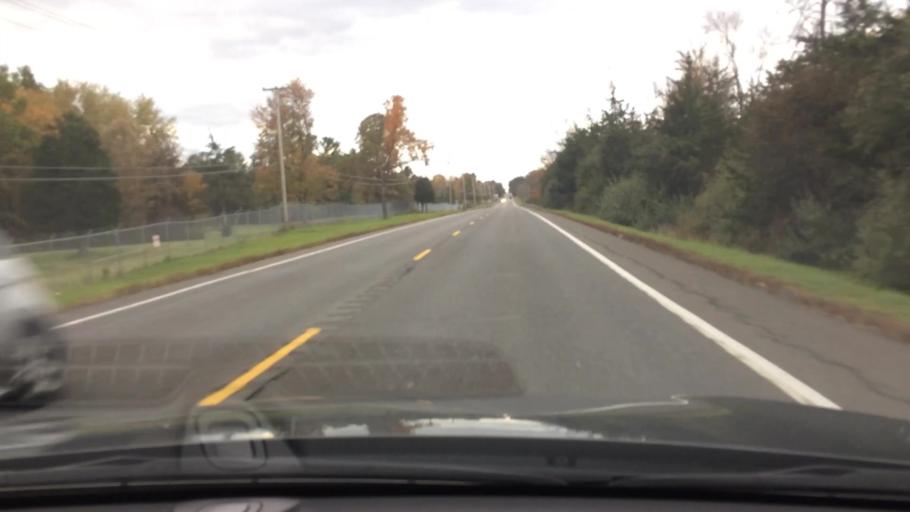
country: US
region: New York
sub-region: Columbia County
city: Stottville
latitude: 42.2927
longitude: -73.7147
